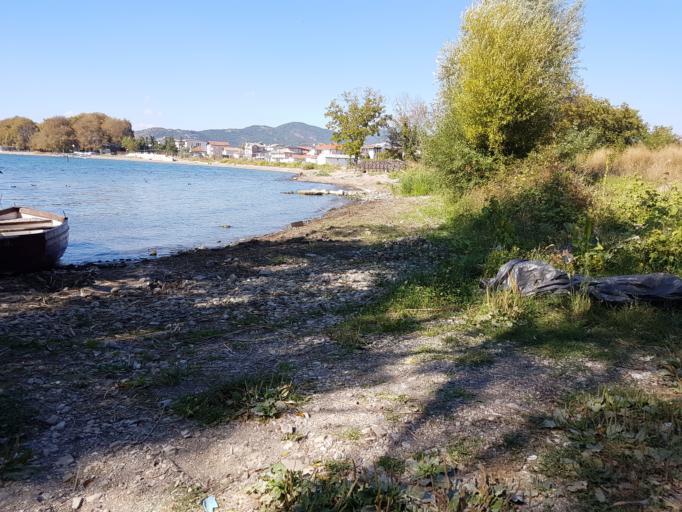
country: MK
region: Ohrid
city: Ohrid
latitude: 41.1162
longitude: 20.7882
